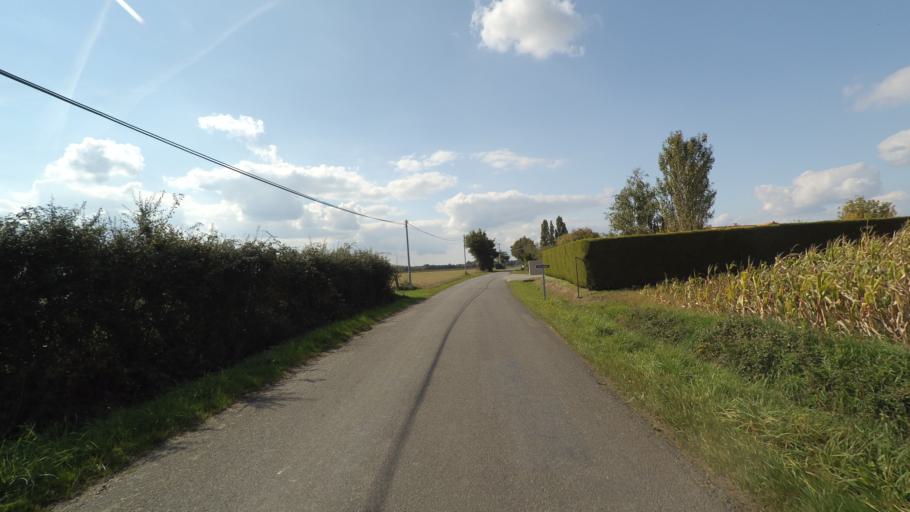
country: FR
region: Pays de la Loire
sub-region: Departement de la Loire-Atlantique
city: Vieillevigne
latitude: 46.9647
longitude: -1.4089
